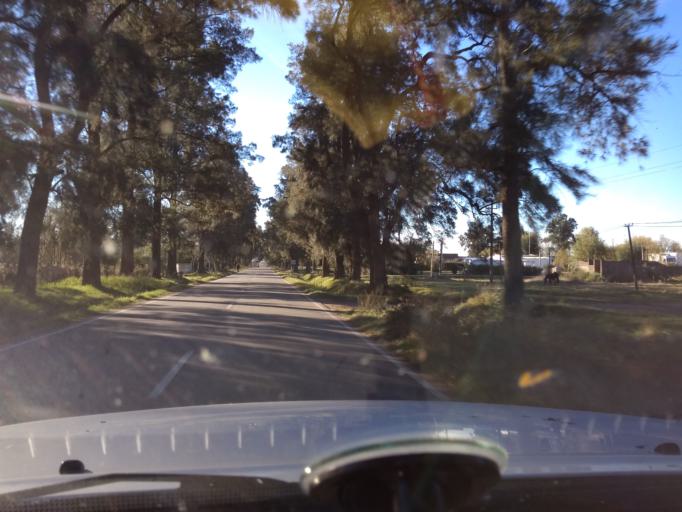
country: UY
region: Canelones
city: San Bautista
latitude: -34.3773
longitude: -55.9594
